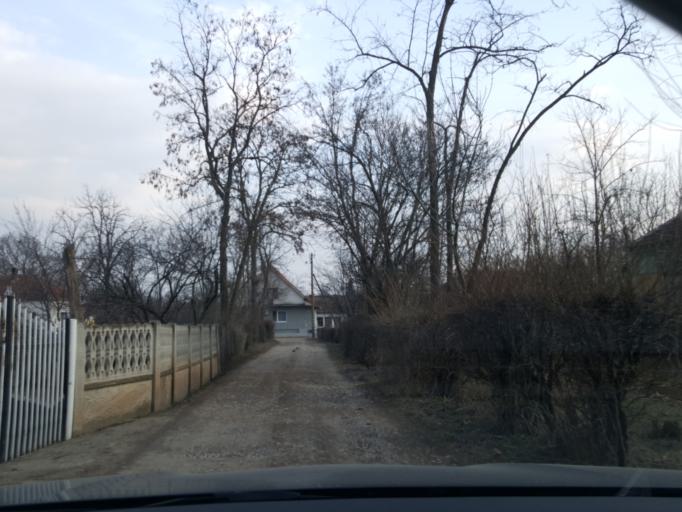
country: RS
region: Central Serbia
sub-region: Nisavski Okrug
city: Razanj
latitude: 43.5929
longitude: 21.6160
